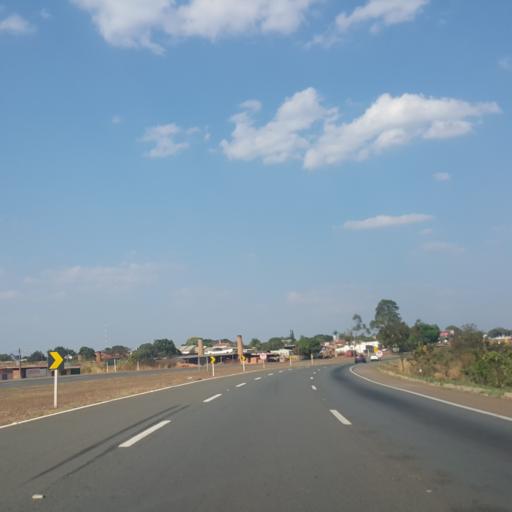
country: BR
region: Goias
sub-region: Abadiania
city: Abadiania
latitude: -16.1879
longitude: -48.7191
